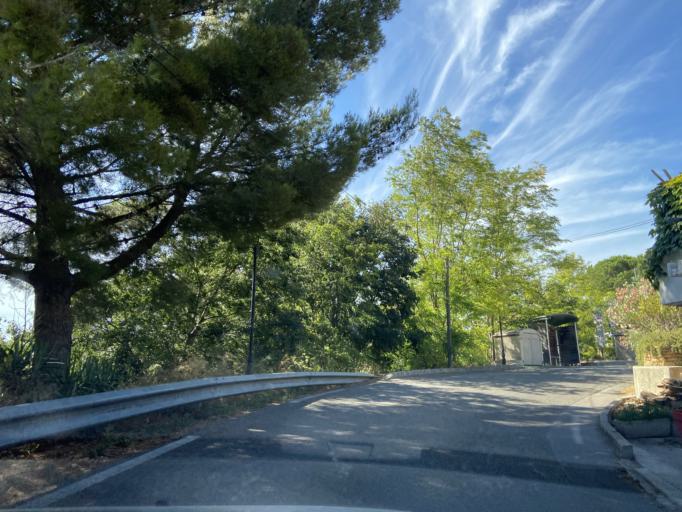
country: FR
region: Provence-Alpes-Cote d'Azur
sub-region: Departement des Bouches-du-Rhone
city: Saint-Chamas
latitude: 43.5630
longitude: 5.0234
